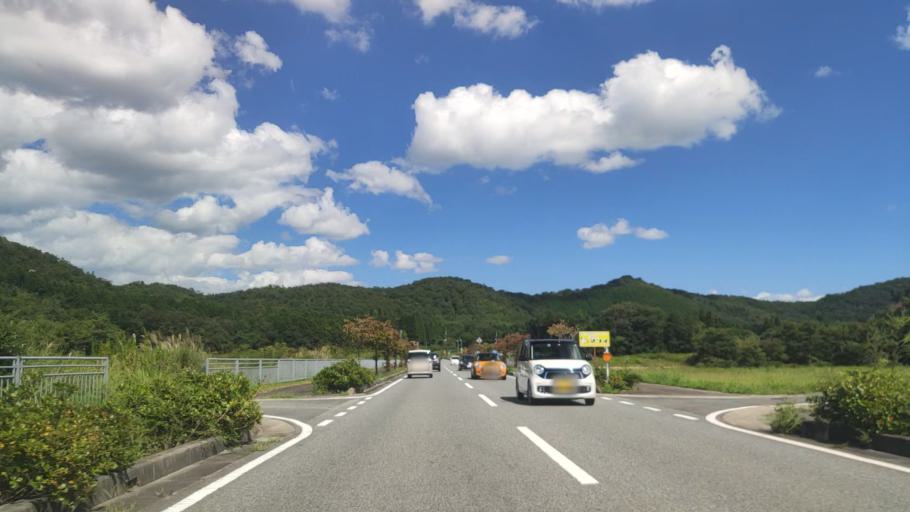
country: JP
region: Kyoto
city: Fukuchiyama
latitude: 35.2557
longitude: 135.1436
